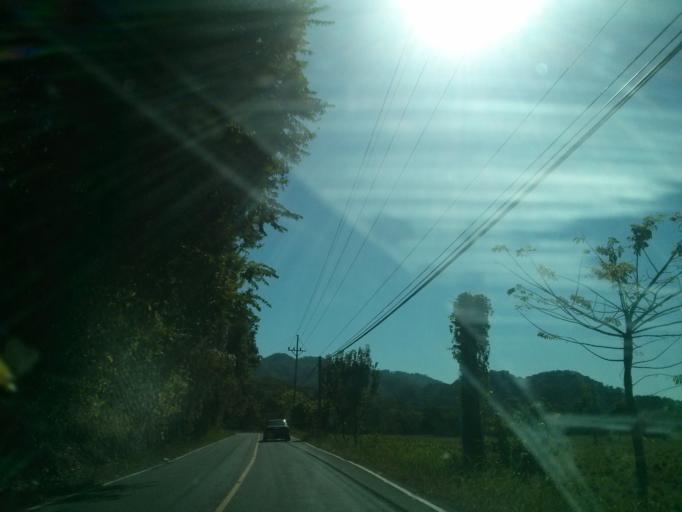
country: CR
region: Puntarenas
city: Paquera
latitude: 9.7541
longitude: -84.9959
